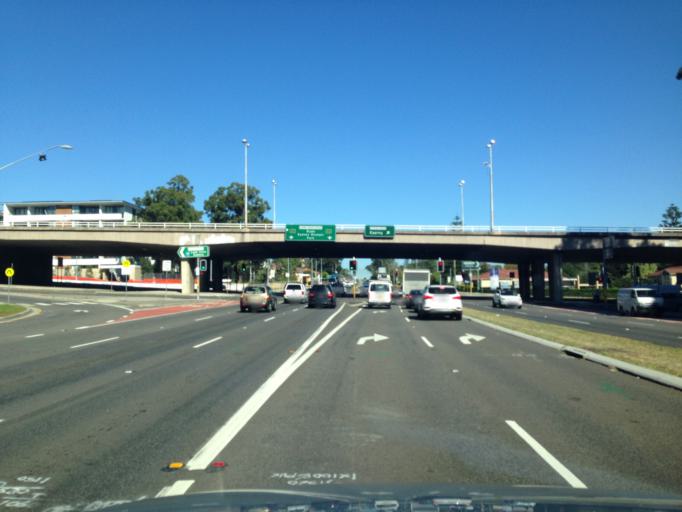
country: AU
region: New South Wales
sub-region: Ryde
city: North Ryde
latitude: -33.7870
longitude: 151.1265
